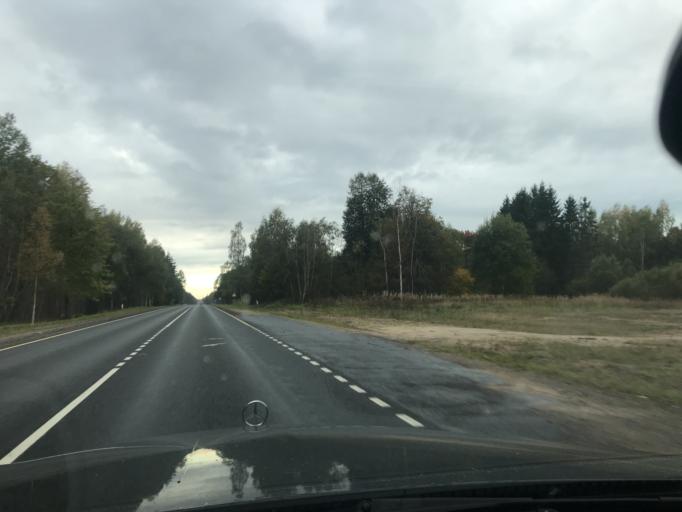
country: RU
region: Pskov
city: Izborsk
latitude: 57.7030
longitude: 27.7915
